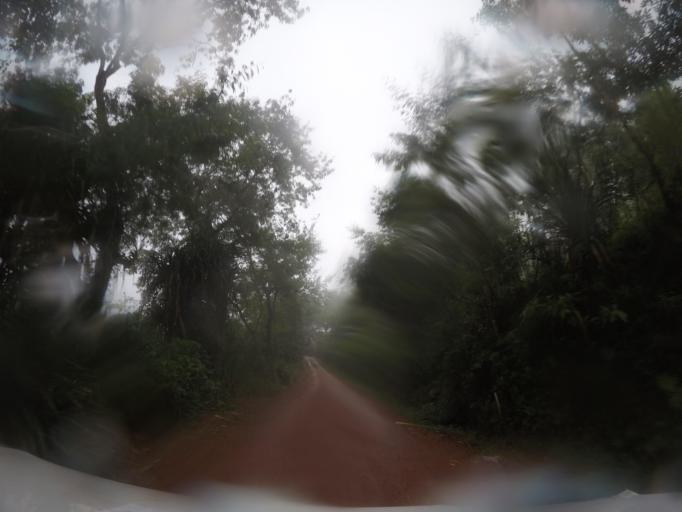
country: TL
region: Baucau
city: Venilale
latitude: -8.6379
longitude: 126.4138
